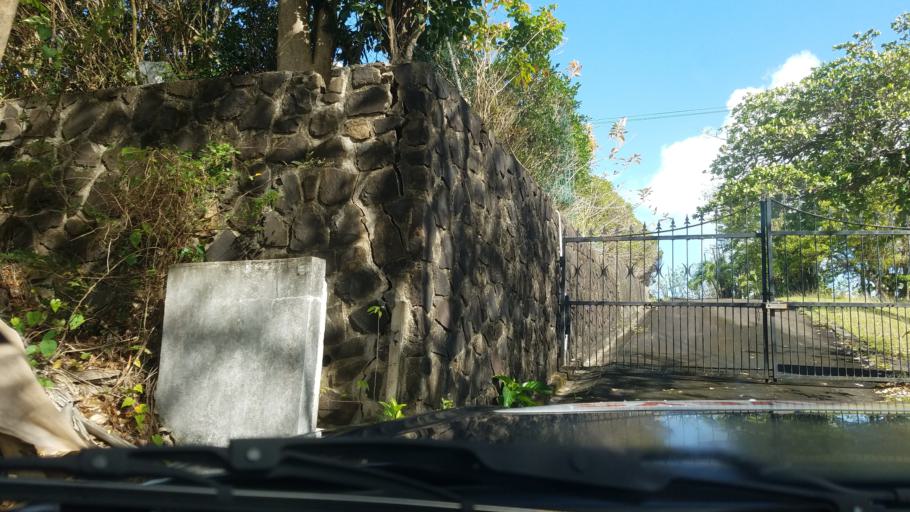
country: LC
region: Castries Quarter
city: Bisee
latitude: 14.0239
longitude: -61.0012
